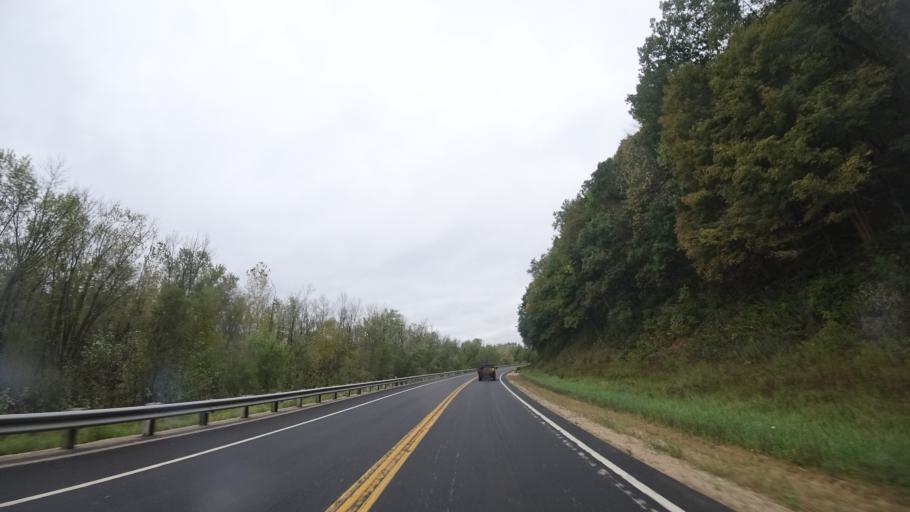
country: US
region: Wisconsin
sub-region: Grant County
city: Boscobel
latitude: 43.1425
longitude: -90.7348
